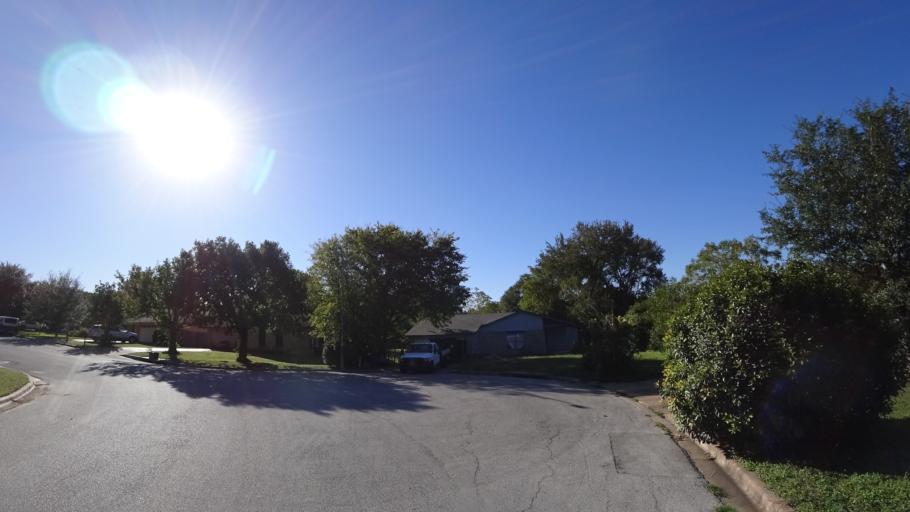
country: US
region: Texas
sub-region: Travis County
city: Austin
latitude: 30.3043
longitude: -97.6664
